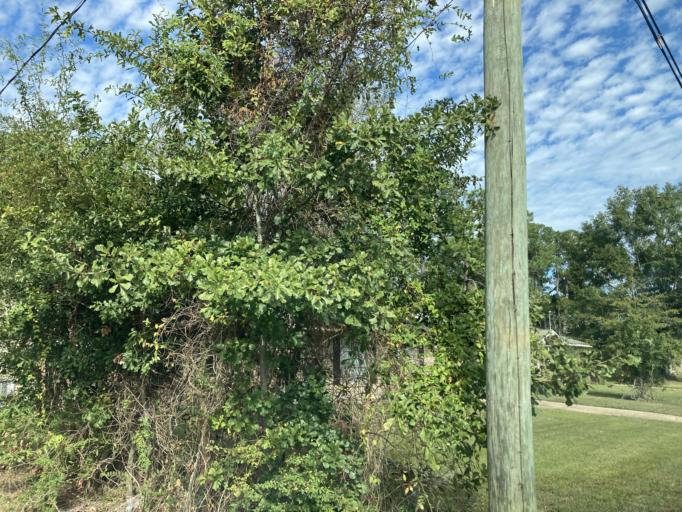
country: US
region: Mississippi
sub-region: Jackson County
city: Saint Martin
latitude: 30.4462
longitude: -88.8703
